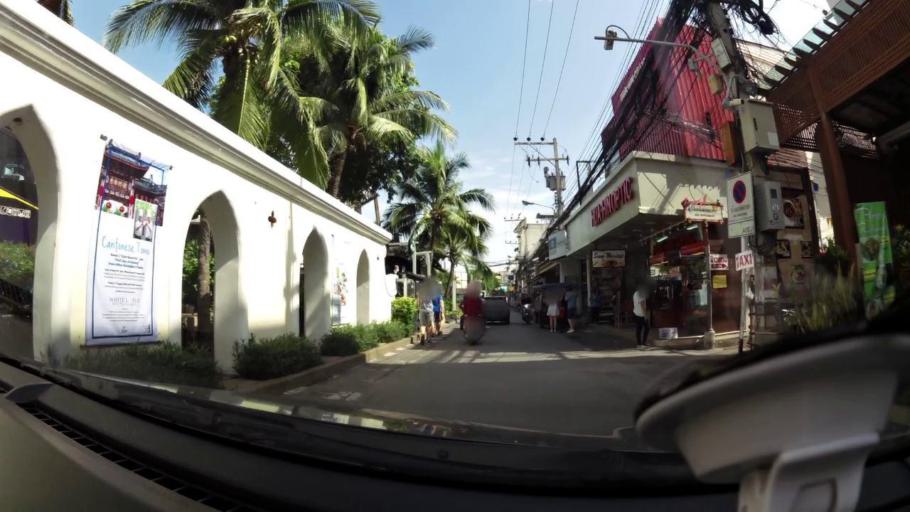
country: TH
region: Prachuap Khiri Khan
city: Hua Hin
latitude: 12.5703
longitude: 99.9600
